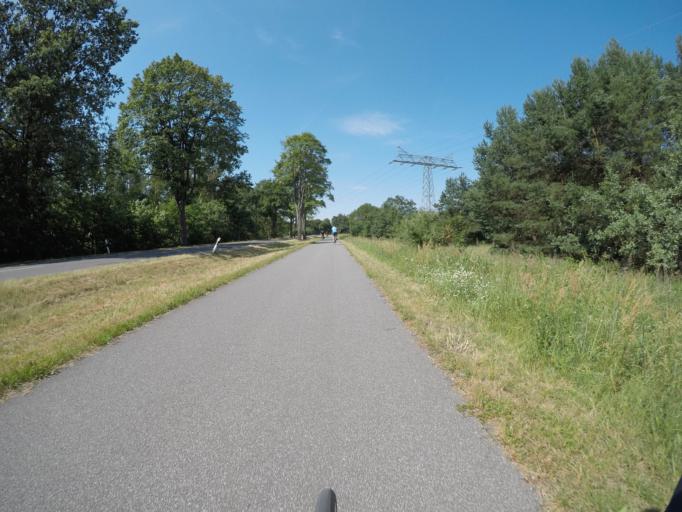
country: DE
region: Berlin
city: Buch
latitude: 52.6788
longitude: 13.5177
